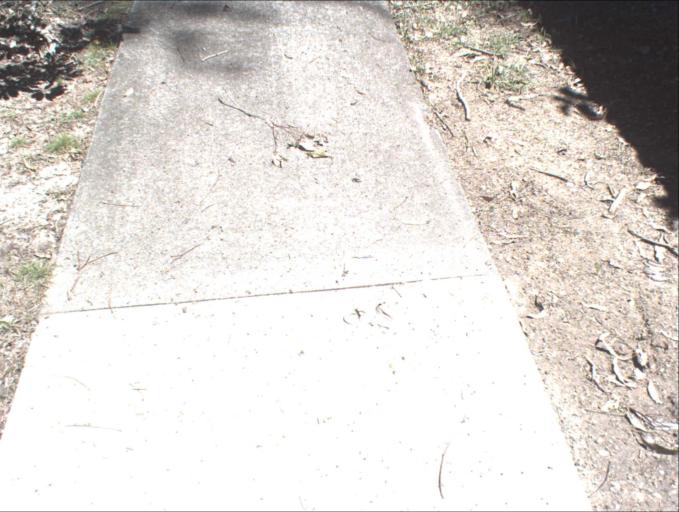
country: AU
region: Queensland
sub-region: Brisbane
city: Forest Lake
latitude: -27.6627
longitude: 153.0060
